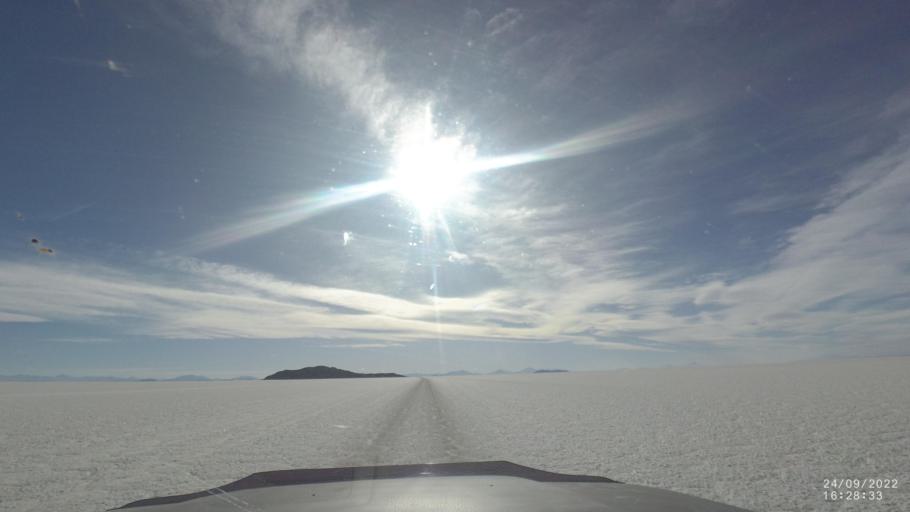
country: BO
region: Potosi
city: Colchani
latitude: -20.2419
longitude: -67.6011
